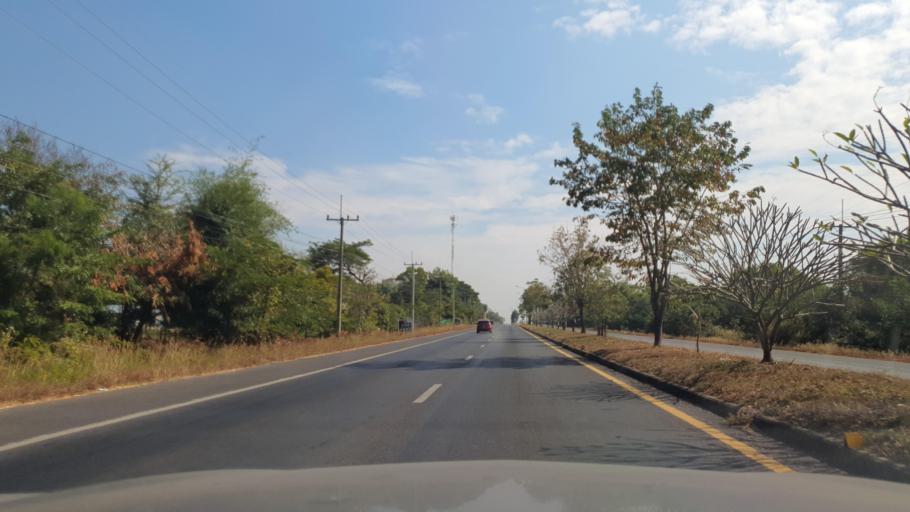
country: TH
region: Maha Sarakham
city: Kantharawichai
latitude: 16.3899
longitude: 103.2688
